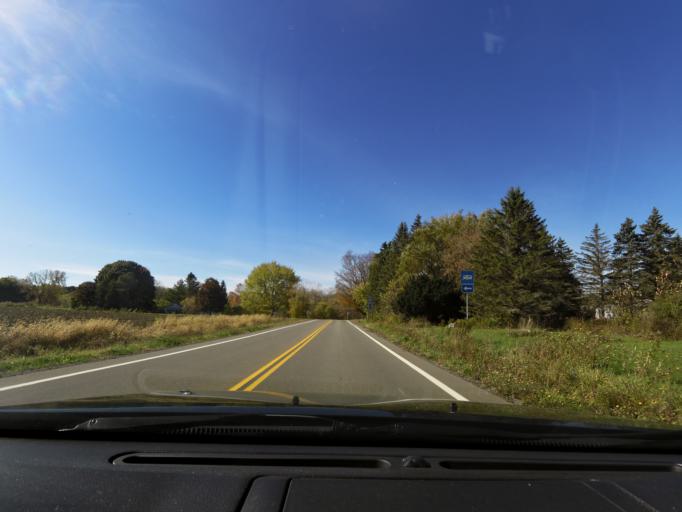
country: US
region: New York
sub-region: Wyoming County
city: Castile
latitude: 42.5926
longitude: -78.1017
